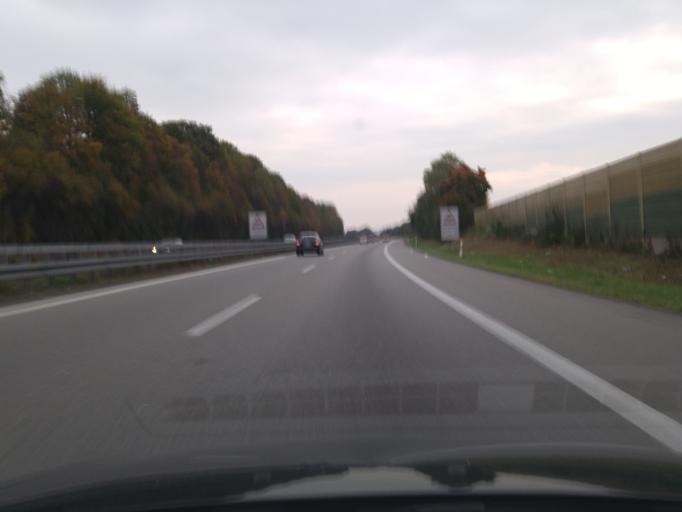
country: DE
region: Baden-Wuerttemberg
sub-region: Regierungsbezirk Stuttgart
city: Bretzfeld
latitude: 49.1737
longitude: 9.3869
